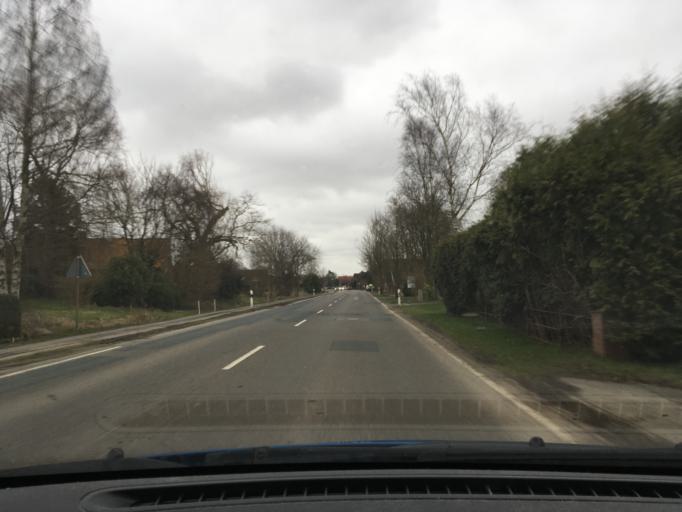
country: DE
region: Schleswig-Holstein
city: Escheburg
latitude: 53.4249
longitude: 10.3208
